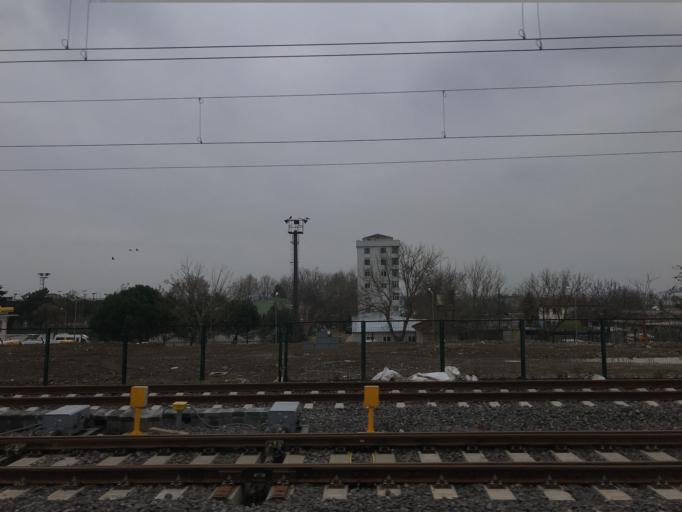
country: TR
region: Istanbul
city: Pendik
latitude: 40.8827
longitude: 29.2145
